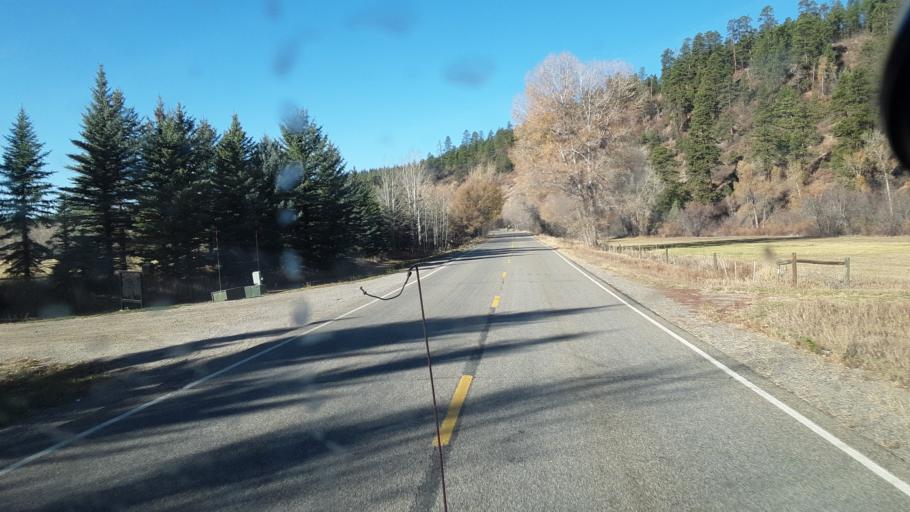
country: US
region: Colorado
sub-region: La Plata County
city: Durango
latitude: 37.3254
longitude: -107.7570
